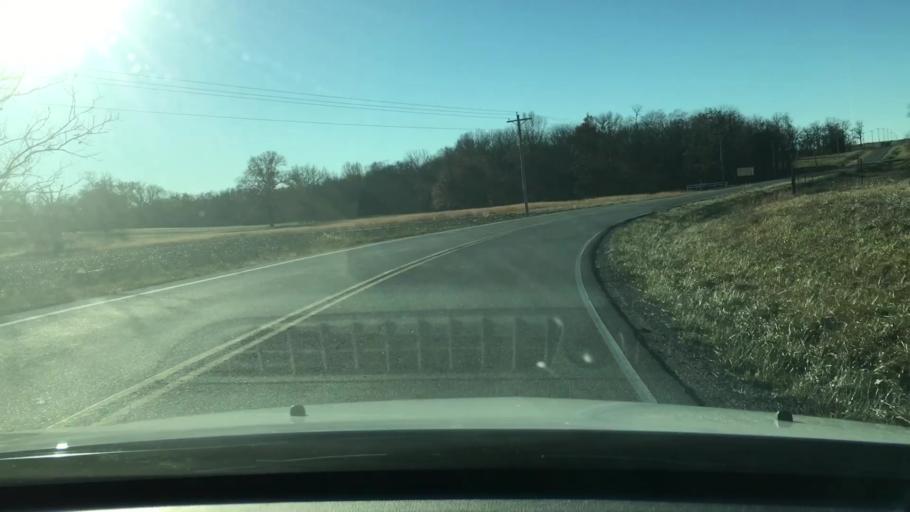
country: US
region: Missouri
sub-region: Audrain County
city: Mexico
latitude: 39.2768
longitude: -91.7785
